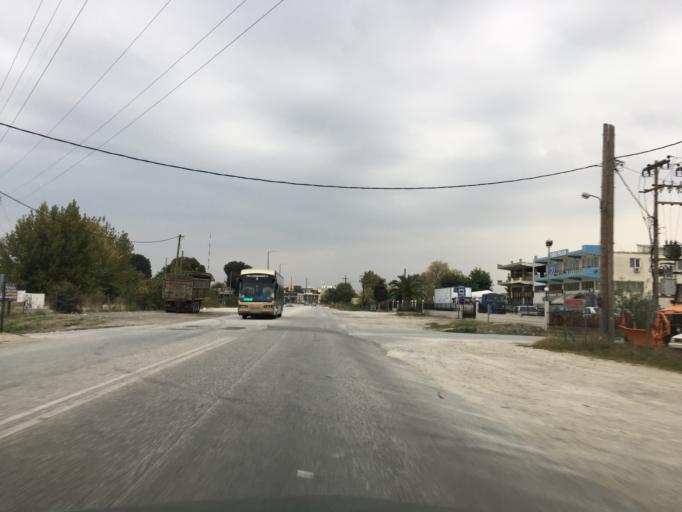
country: GR
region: Thessaly
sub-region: Trikala
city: Trikala
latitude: 39.5584
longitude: 21.7845
